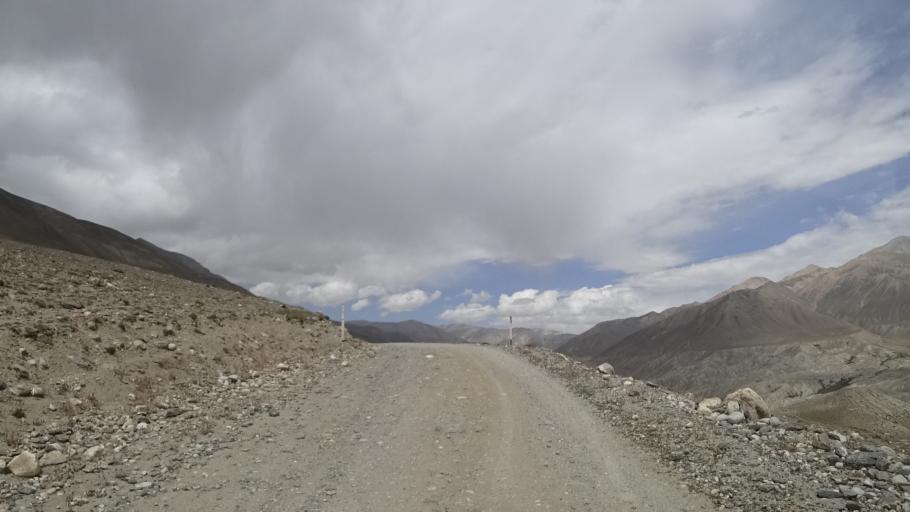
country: AF
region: Badakhshan
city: Khandud
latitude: 37.1417
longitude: 72.7379
